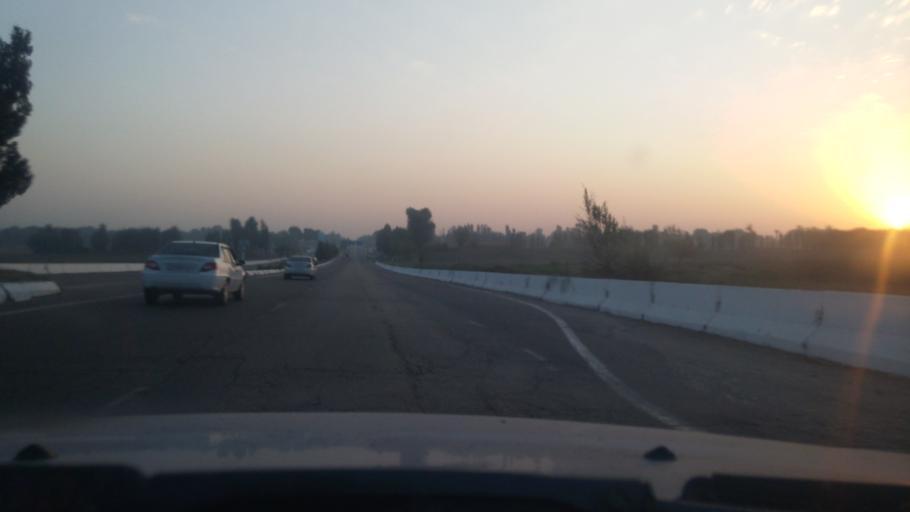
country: UZ
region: Toshkent
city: Amir Timur
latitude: 41.0474
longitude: 68.8911
